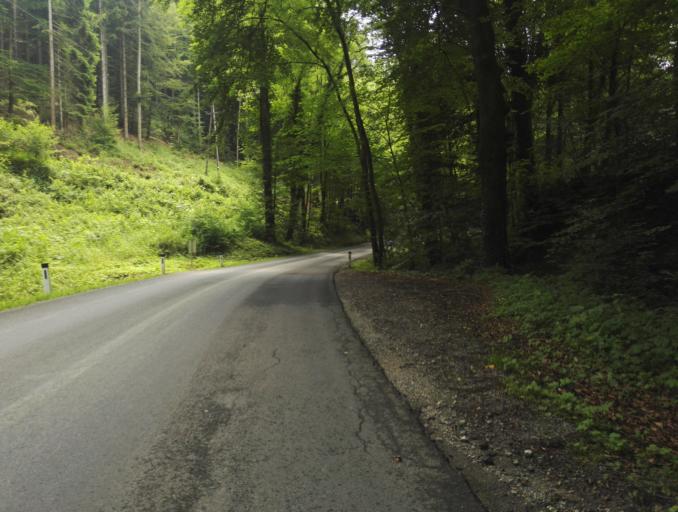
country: AT
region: Styria
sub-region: Politischer Bezirk Graz-Umgebung
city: Gratwein
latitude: 47.0936
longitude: 15.3168
